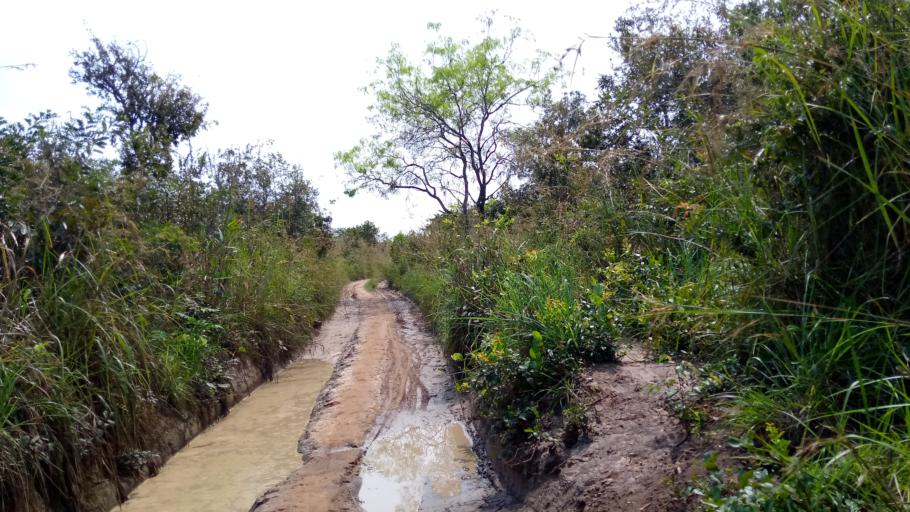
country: CD
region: Bandundu
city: Bandundu
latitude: -4.1323
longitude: 17.4150
